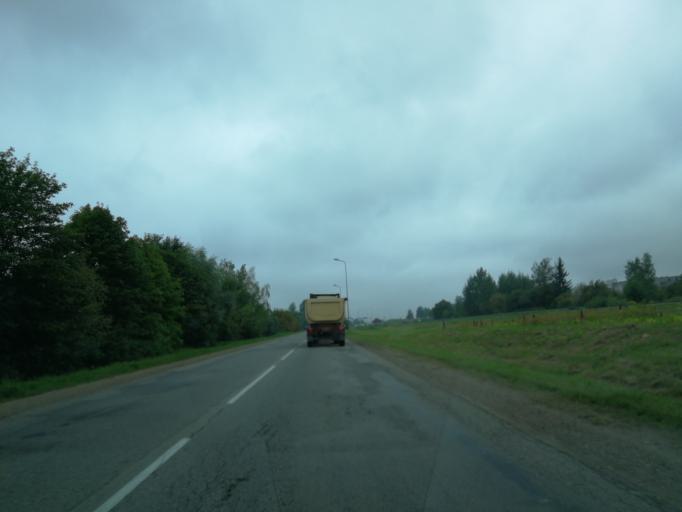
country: LV
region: Jekabpils Rajons
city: Jekabpils
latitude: 56.5025
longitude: 25.8951
